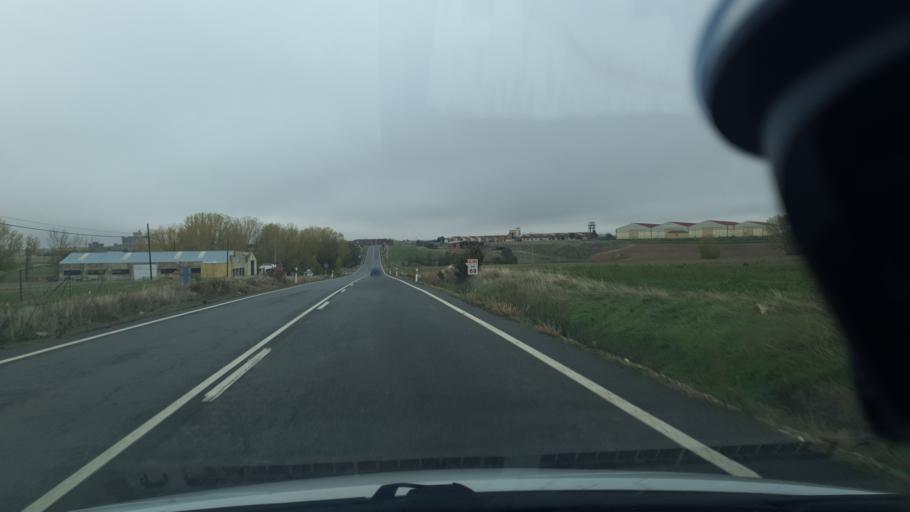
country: ES
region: Castille and Leon
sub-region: Provincia de Segovia
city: Turegano
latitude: 41.1522
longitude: -4.0191
